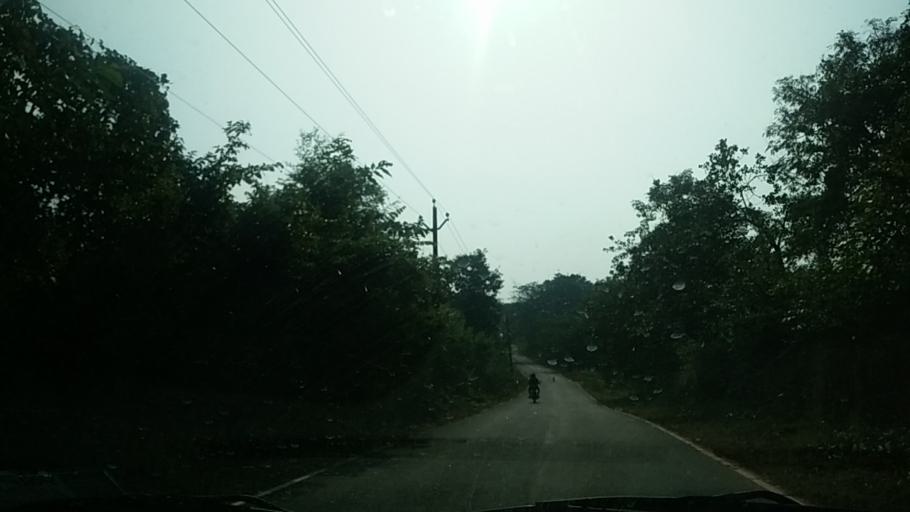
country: IN
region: Goa
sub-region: South Goa
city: Sanguem
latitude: 15.2244
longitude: 74.1897
